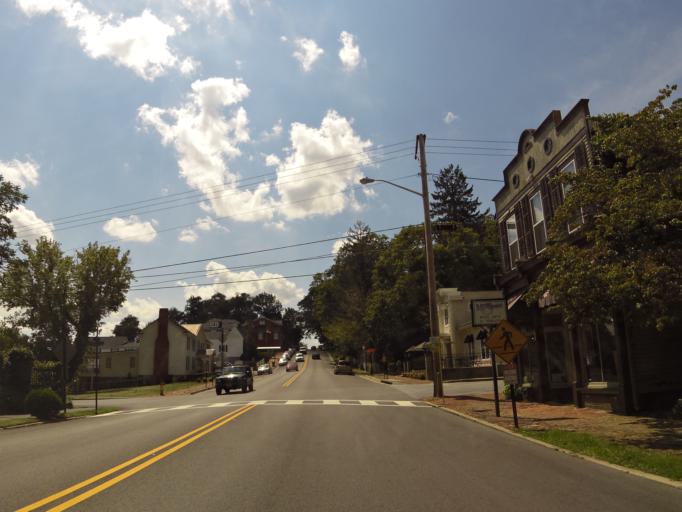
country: US
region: Virginia
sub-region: Washington County
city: Abingdon
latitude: 36.7133
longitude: -81.9670
